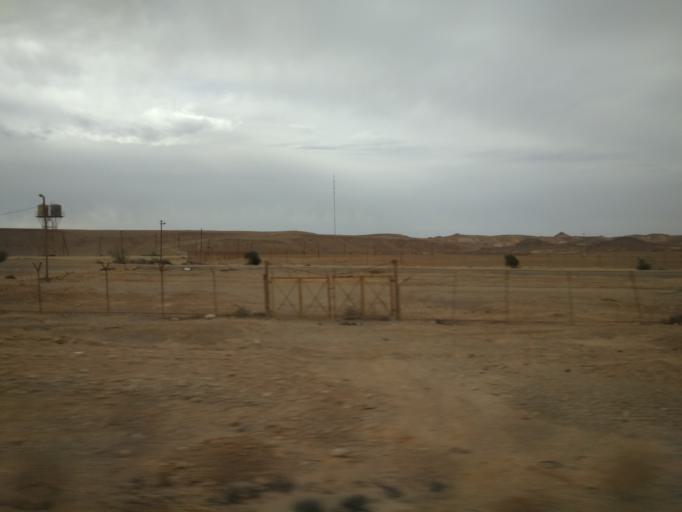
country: IL
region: Southern District
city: Eilat
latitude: 29.8587
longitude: 34.8456
